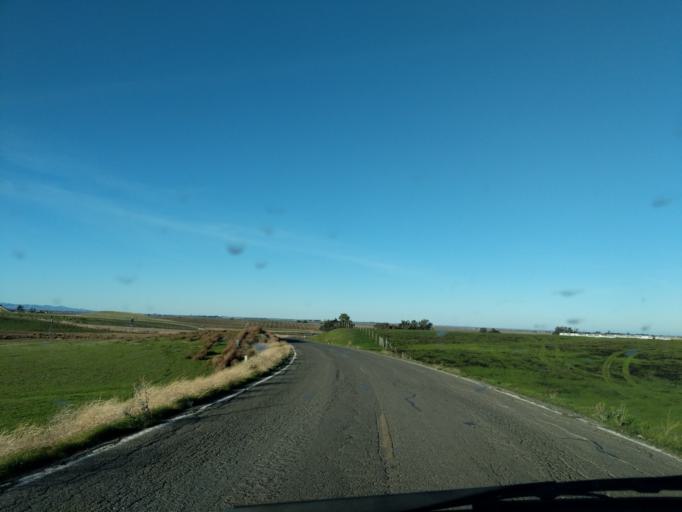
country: US
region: California
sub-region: Merced County
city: Los Banos
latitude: 37.0527
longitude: -120.9545
